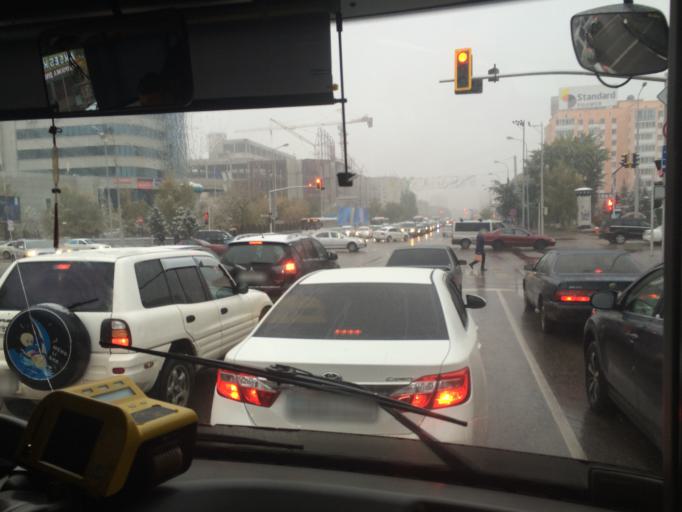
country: KZ
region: Astana Qalasy
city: Astana
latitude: 51.1659
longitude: 71.4269
